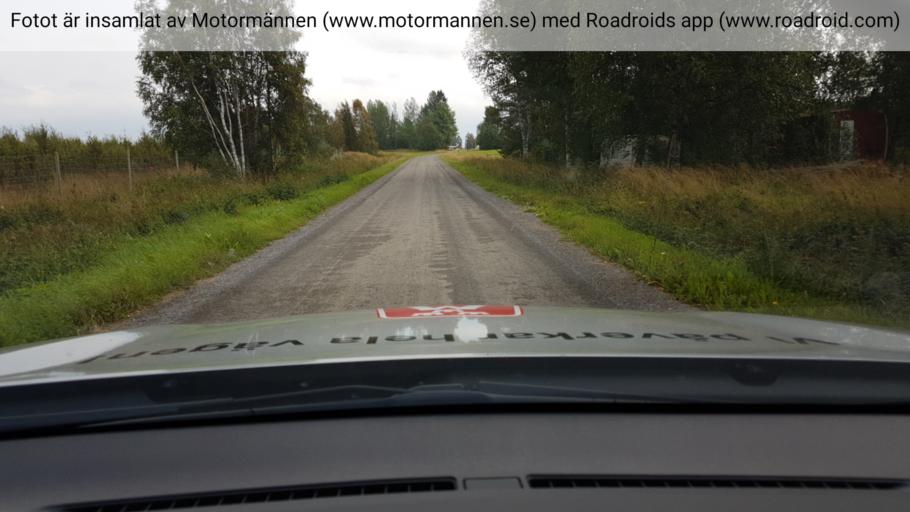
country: SE
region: Jaemtland
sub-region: Stroemsunds Kommun
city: Stroemsund
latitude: 63.7301
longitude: 15.4727
